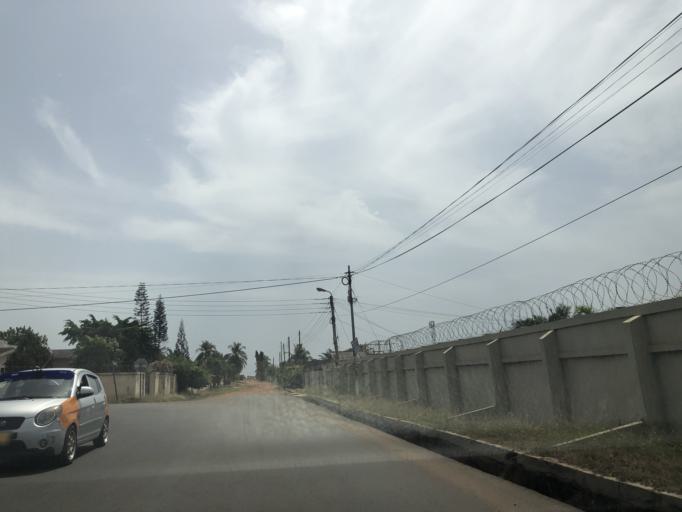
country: GH
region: Greater Accra
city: Dome
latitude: 5.6208
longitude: -0.2502
